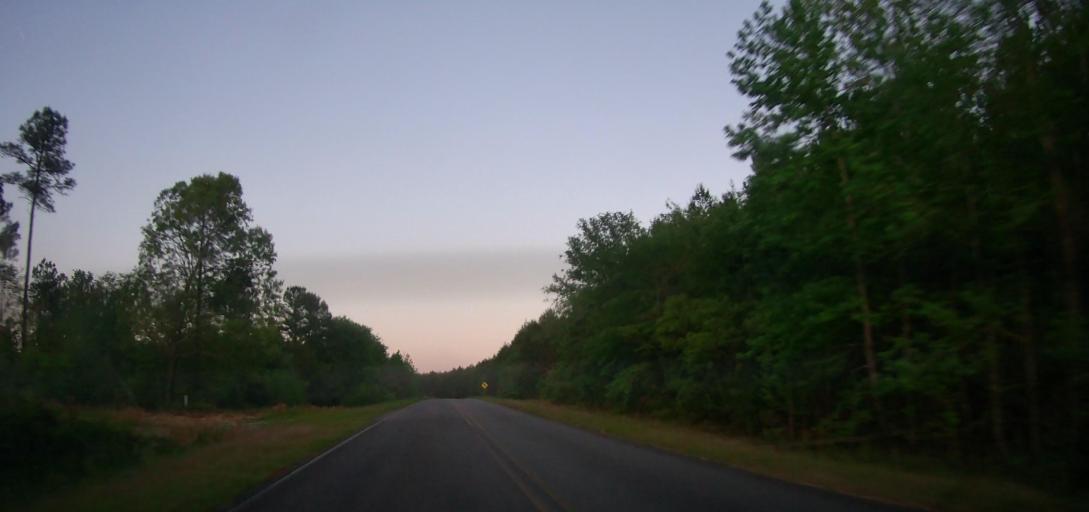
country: US
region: Georgia
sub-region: Marion County
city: Buena Vista
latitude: 32.2590
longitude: -84.5688
